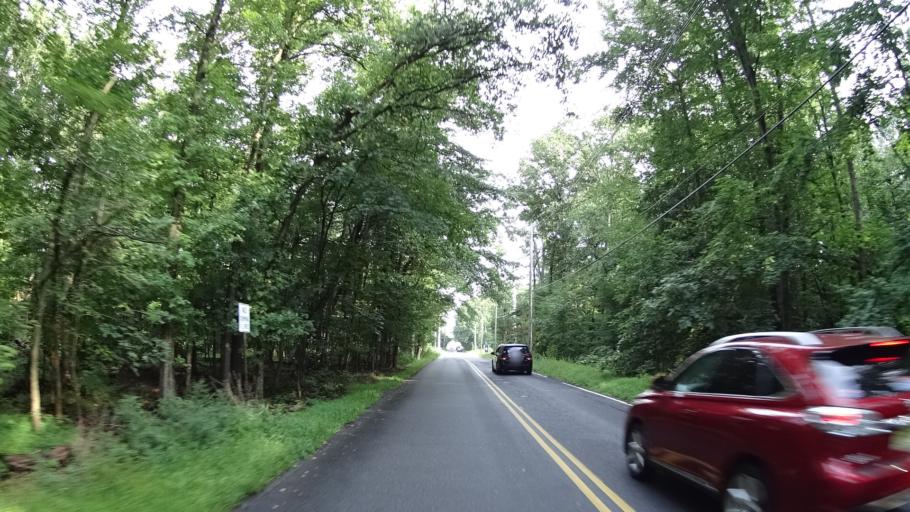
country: US
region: New Jersey
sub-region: Union County
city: New Providence
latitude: 40.7009
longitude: -74.4255
